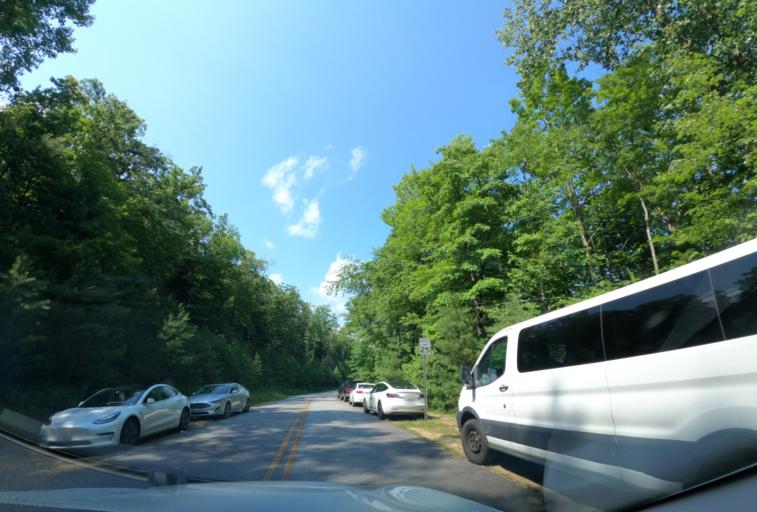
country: US
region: North Carolina
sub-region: Transylvania County
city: Brevard
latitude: 35.0900
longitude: -82.9504
